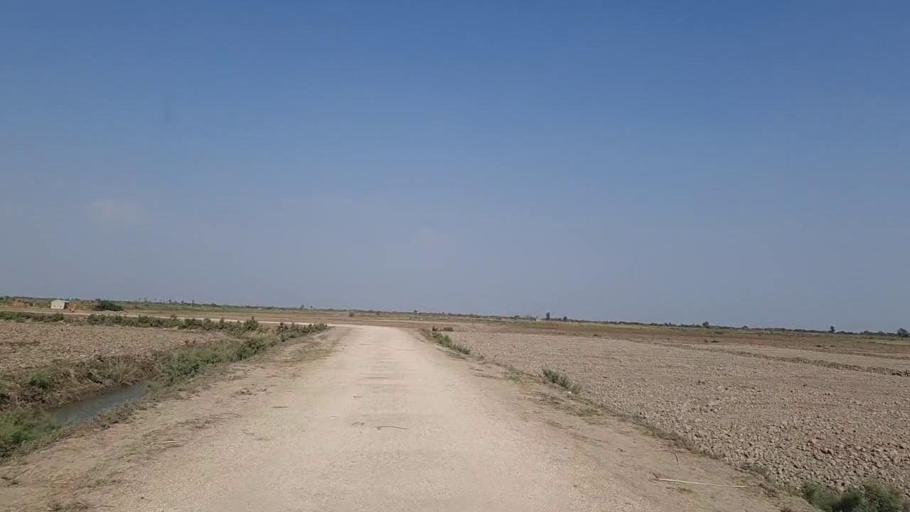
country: PK
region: Sindh
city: Daro Mehar
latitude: 24.7595
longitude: 68.1655
